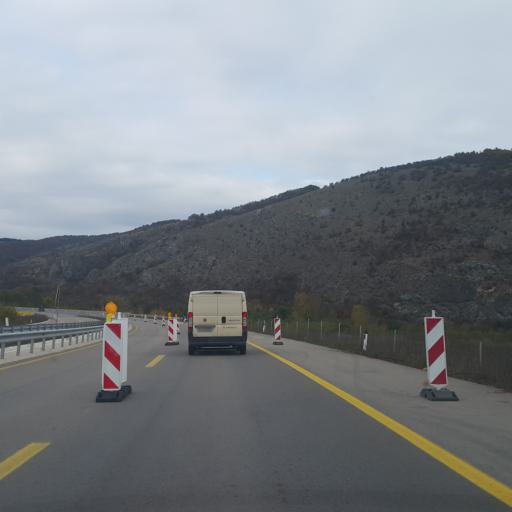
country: RS
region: Central Serbia
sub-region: Pirotski Okrug
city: Bela Palanka
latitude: 43.2322
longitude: 22.3790
